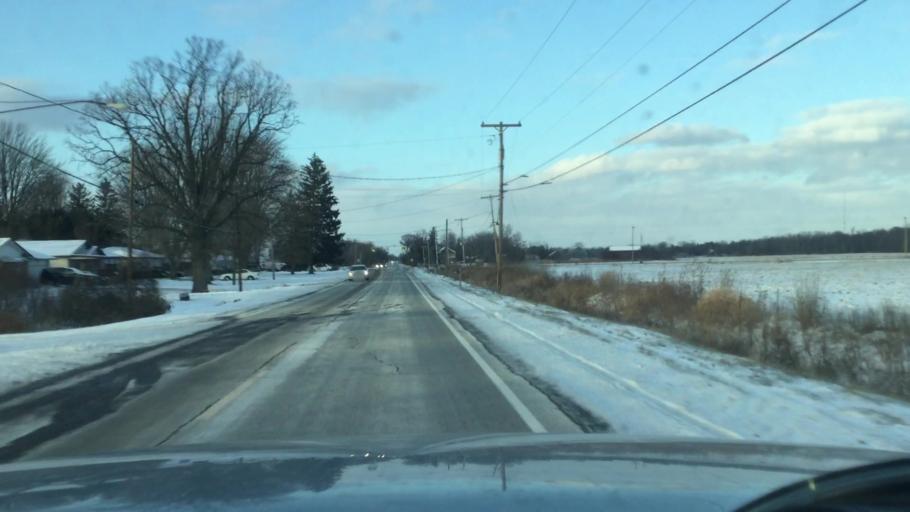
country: US
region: Michigan
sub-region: Saginaw County
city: Saginaw
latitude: 43.3743
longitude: -83.9353
